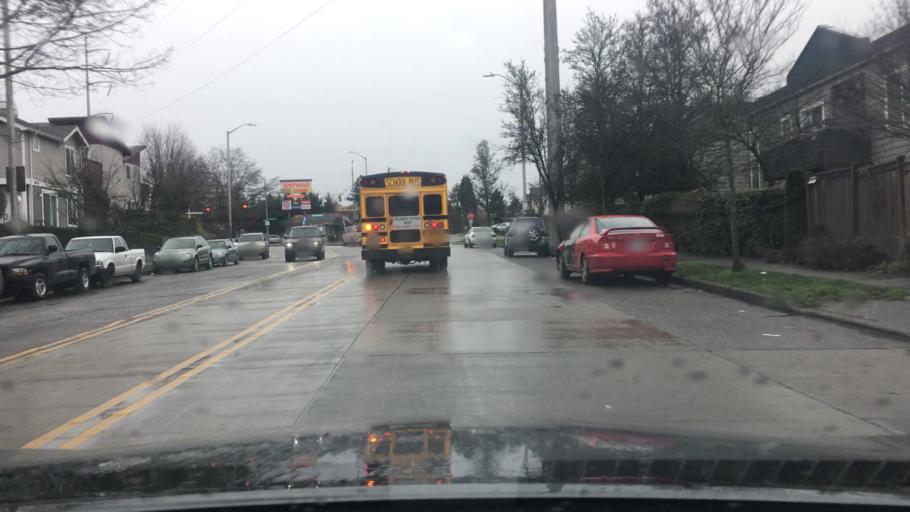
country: US
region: Washington
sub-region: King County
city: White Center
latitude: 47.5240
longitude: -122.3605
